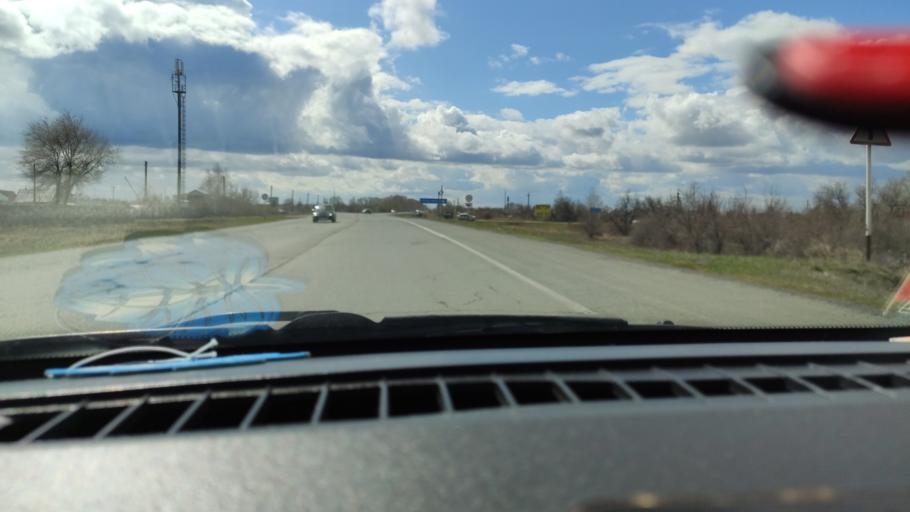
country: RU
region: Samara
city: Tol'yatti
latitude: 53.7112
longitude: 49.4235
